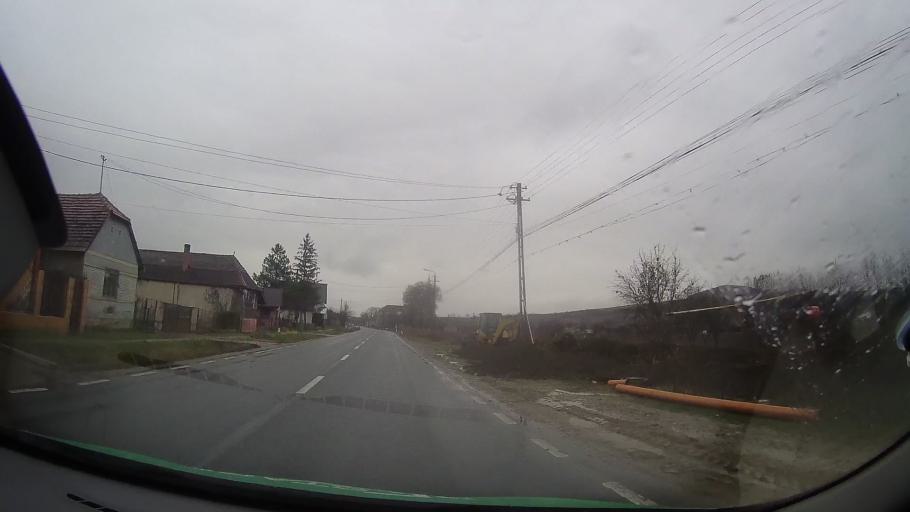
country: RO
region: Bistrita-Nasaud
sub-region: Comuna Galatii Bistritei
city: Galatii Bistritei
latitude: 46.9731
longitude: 24.4331
